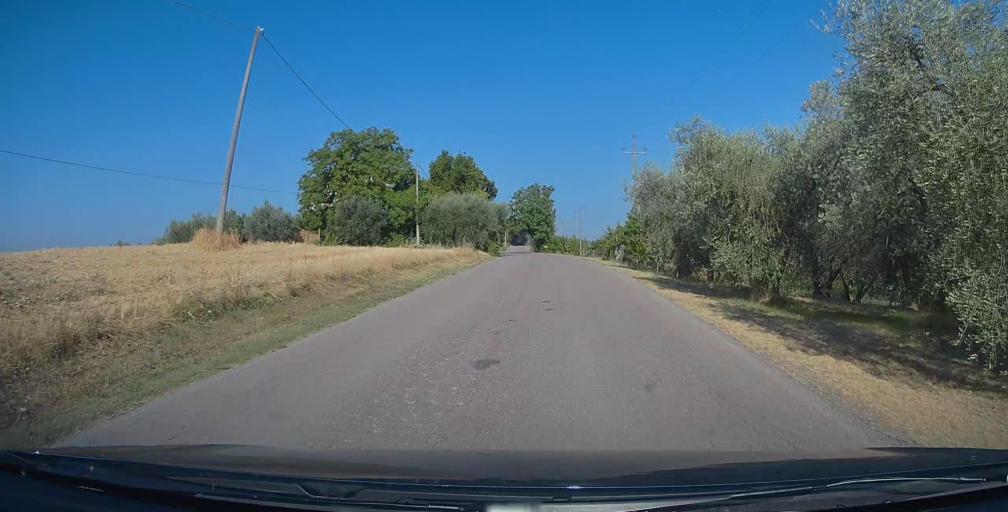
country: IT
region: Umbria
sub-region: Provincia di Terni
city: Otricoli
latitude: 42.4067
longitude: 12.5048
